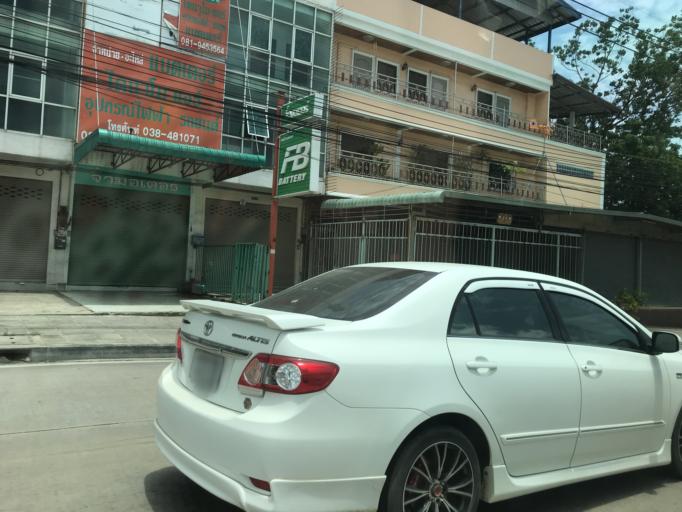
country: TH
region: Chon Buri
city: Ban Talat Bueng
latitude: 13.1111
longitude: 100.9508
